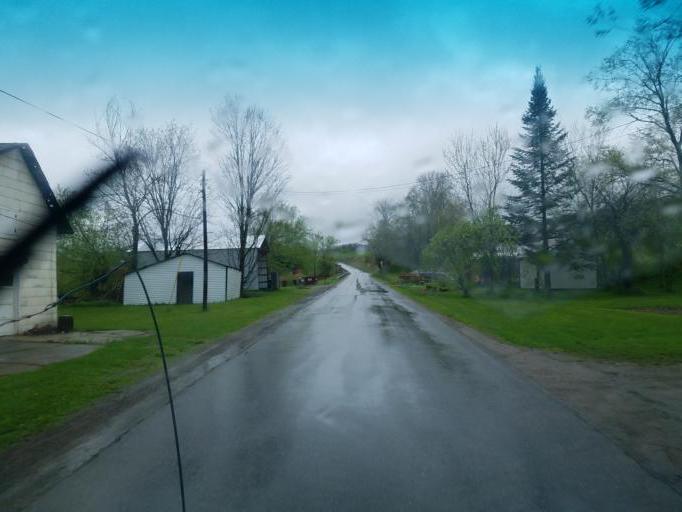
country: US
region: Pennsylvania
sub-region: Tioga County
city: Westfield
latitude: 41.9588
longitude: -77.6477
